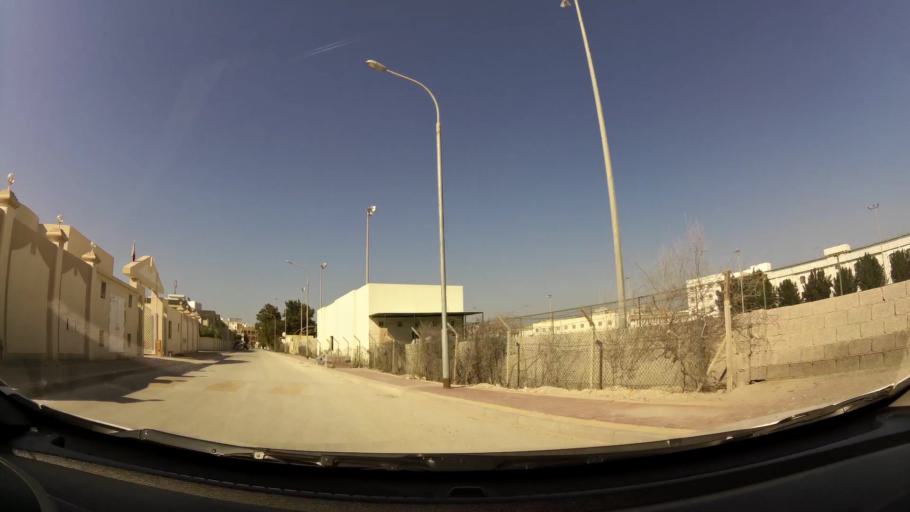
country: BH
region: Manama
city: Manama
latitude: 26.2066
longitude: 50.5714
